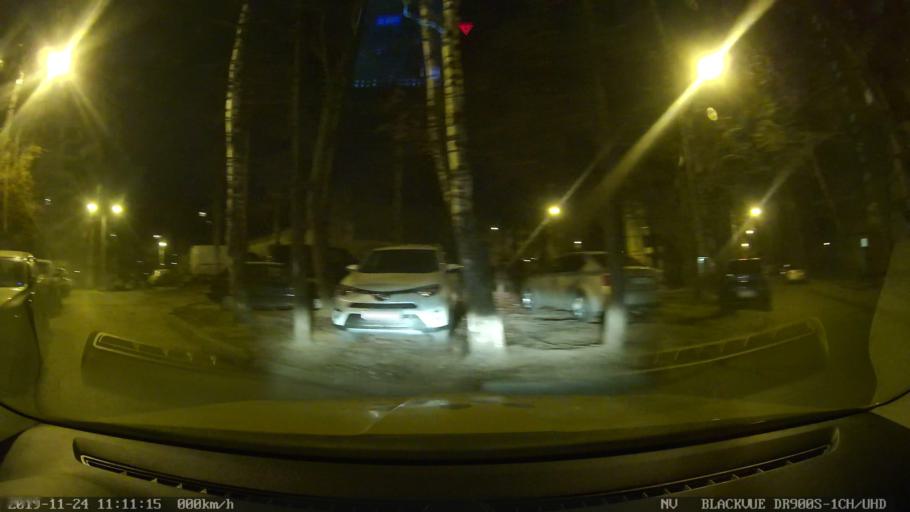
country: RU
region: Moskovskaya
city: Mytishchi
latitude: 55.9028
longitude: 37.7281
